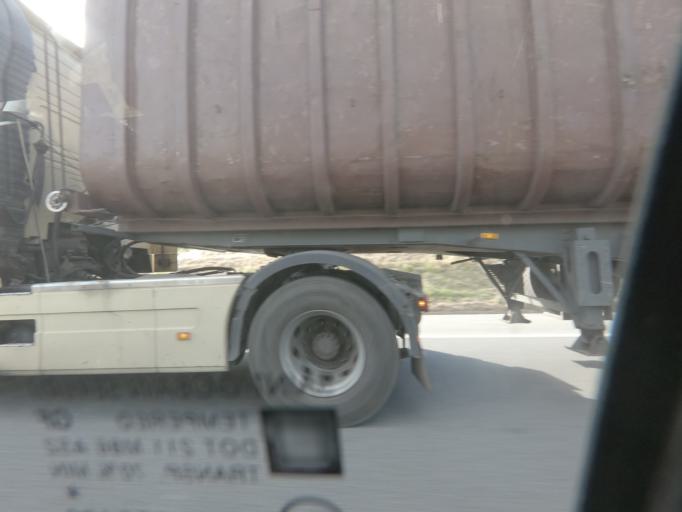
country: PT
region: Porto
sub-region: Penafiel
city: Penafiel
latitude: 41.2060
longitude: -8.2976
